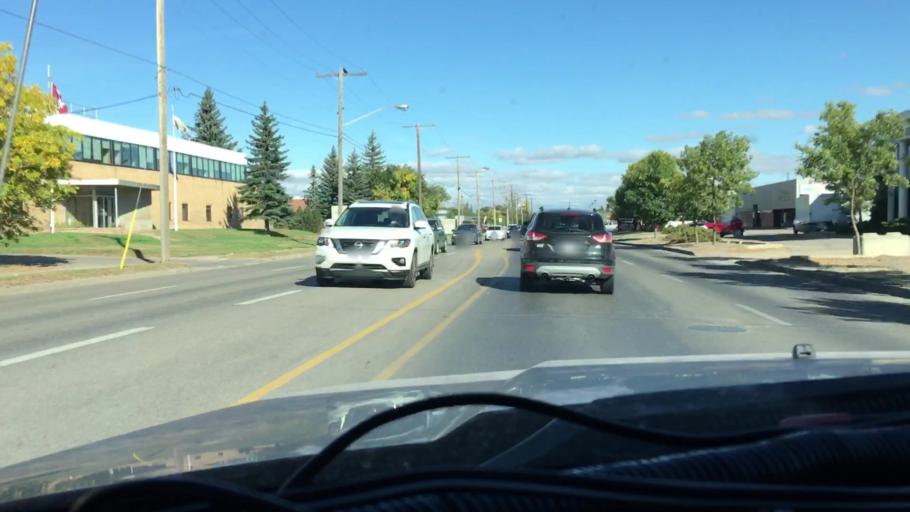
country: CA
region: Saskatchewan
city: Regina
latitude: 50.4629
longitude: -104.6046
